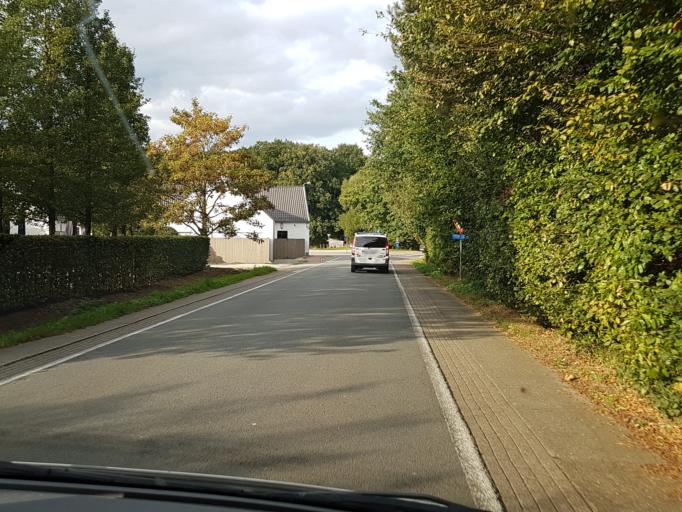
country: BE
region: Flanders
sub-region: Provincie Antwerpen
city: Zandhoven
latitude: 51.2075
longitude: 4.6350
